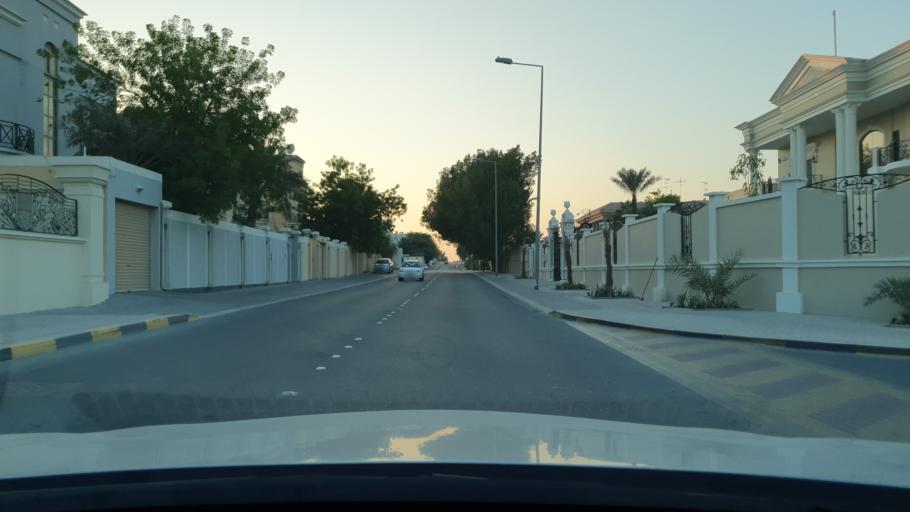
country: BH
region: Northern
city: Ar Rifa'
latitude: 26.1412
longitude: 50.5284
